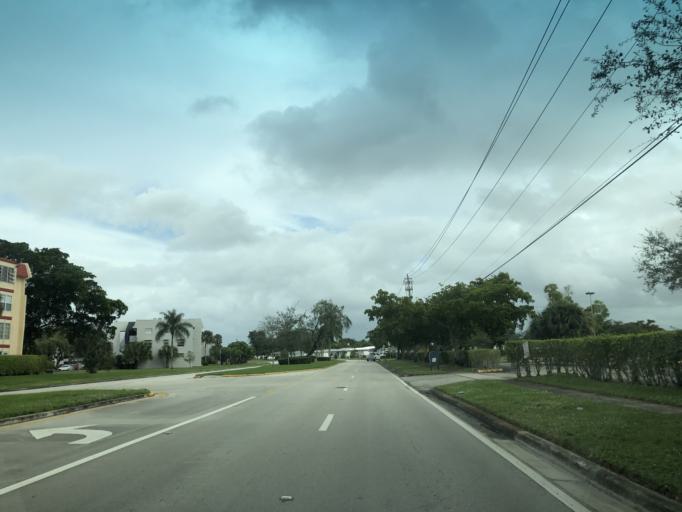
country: US
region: Florida
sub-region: Broward County
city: Margate
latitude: 26.2402
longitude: -80.2282
